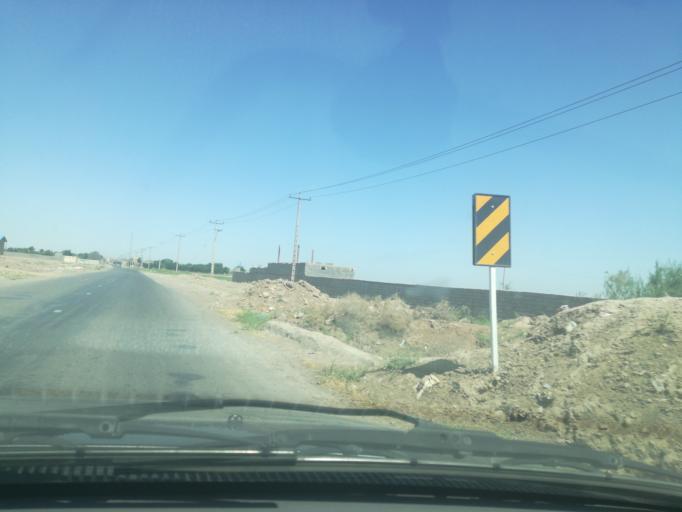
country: IR
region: Razavi Khorasan
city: Sarakhs
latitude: 36.5666
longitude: 61.1412
